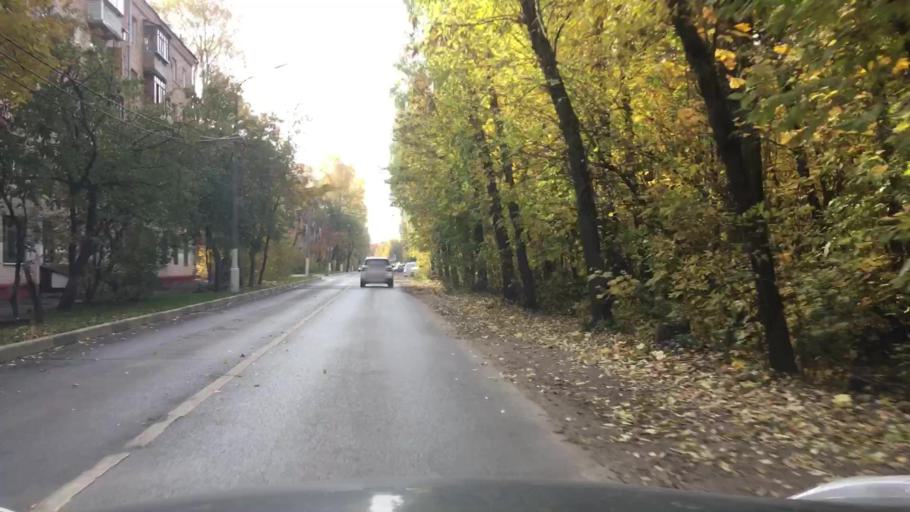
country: RU
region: Moskovskaya
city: Balashikha
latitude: 55.8008
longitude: 37.9271
